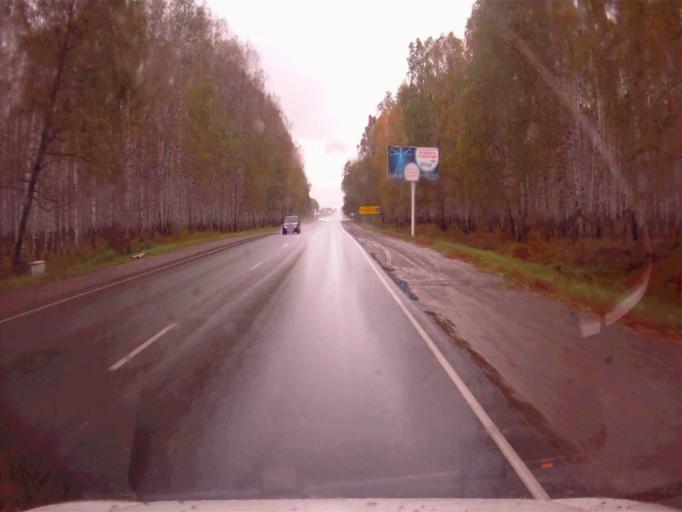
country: RU
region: Chelyabinsk
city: Argayash
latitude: 55.4143
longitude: 61.0334
